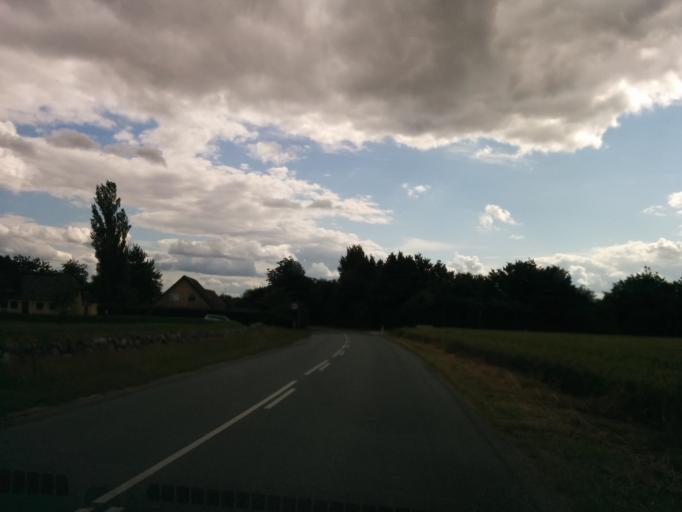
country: DK
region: Central Jutland
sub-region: Arhus Kommune
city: Kolt
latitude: 56.1094
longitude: 10.0685
